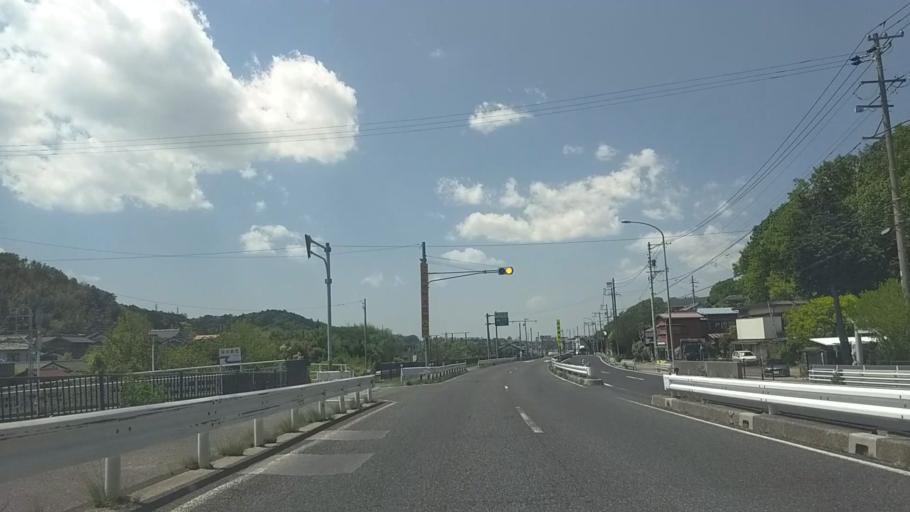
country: JP
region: Aichi
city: Okazaki
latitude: 34.9110
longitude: 137.2263
